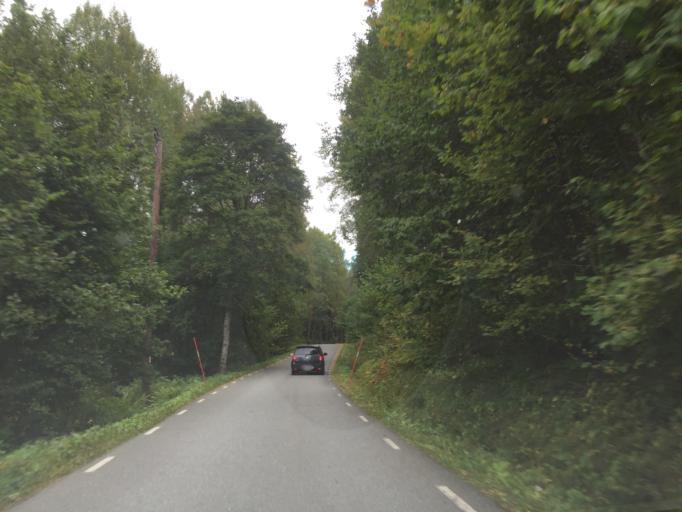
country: SE
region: OErebro
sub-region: Orebro Kommun
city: Hovsta
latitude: 59.3355
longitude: 15.1812
